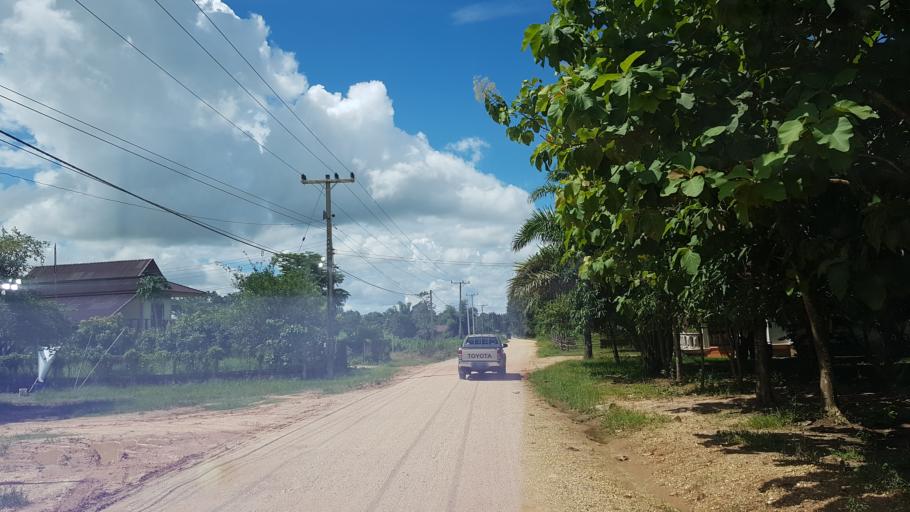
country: LA
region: Vientiane
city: Vientiane
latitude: 18.2191
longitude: 102.5167
